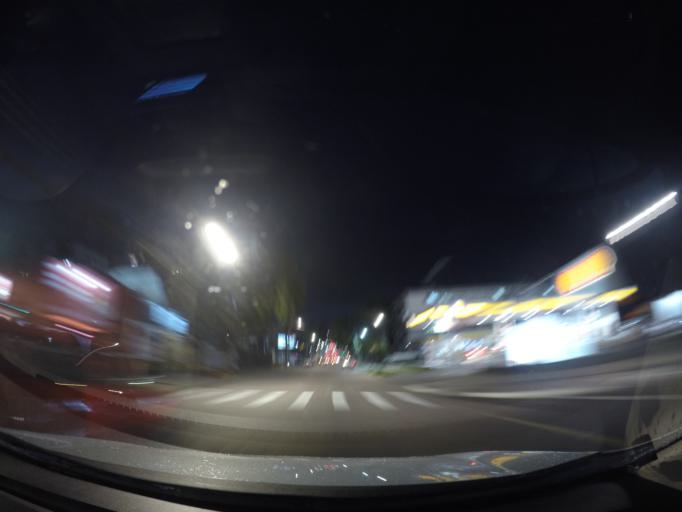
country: BR
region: Parana
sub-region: Curitiba
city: Curitiba
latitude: -25.4486
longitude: -49.2731
